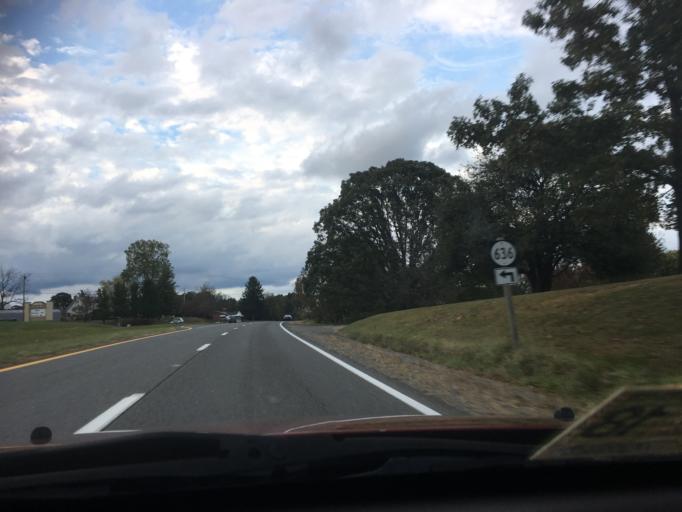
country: US
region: Virginia
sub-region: Pulaski County
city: Dublin
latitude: 37.1154
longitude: -80.6985
